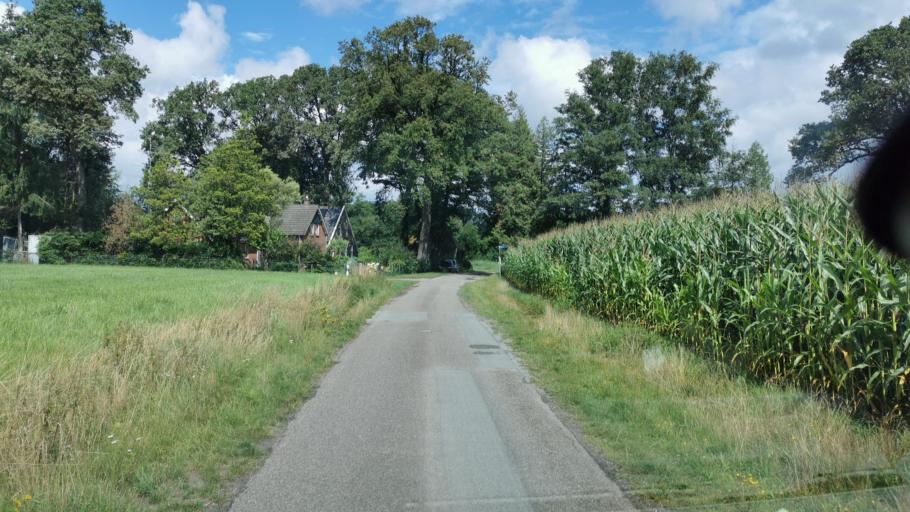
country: NL
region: Overijssel
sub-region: Gemeente Haaksbergen
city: Haaksbergen
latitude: 52.1401
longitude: 6.7387
